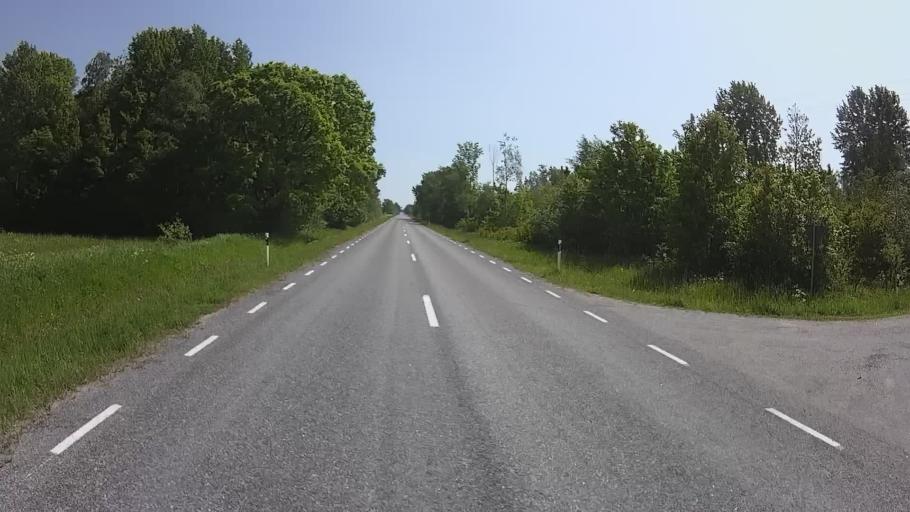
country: EE
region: Saare
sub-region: Kuressaare linn
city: Kuressaare
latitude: 58.3728
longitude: 22.0430
